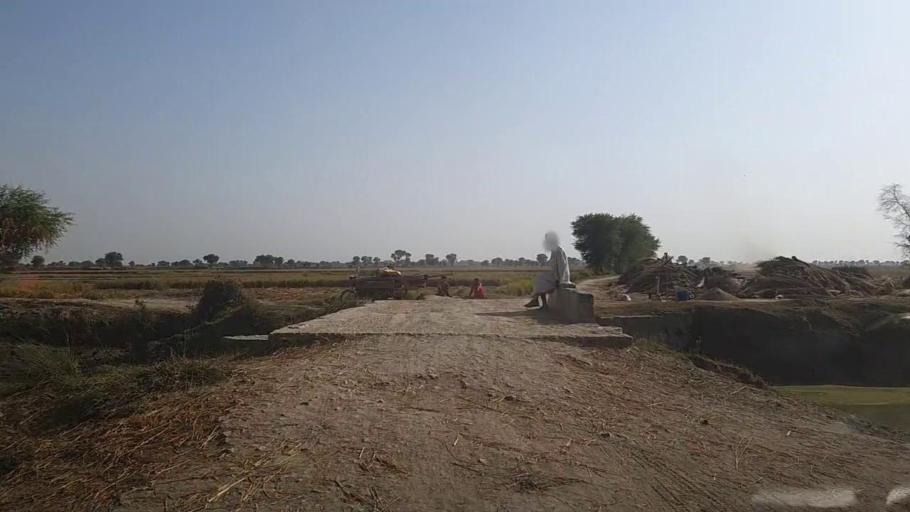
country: PK
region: Sindh
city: Kandhkot
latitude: 28.3511
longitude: 69.3352
